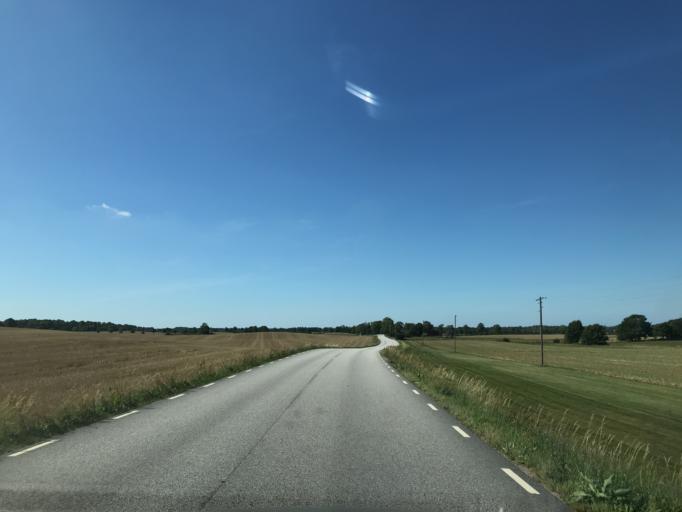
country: SE
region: Skane
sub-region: Tomelilla Kommun
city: Tomelilla
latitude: 55.6446
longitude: 13.9816
